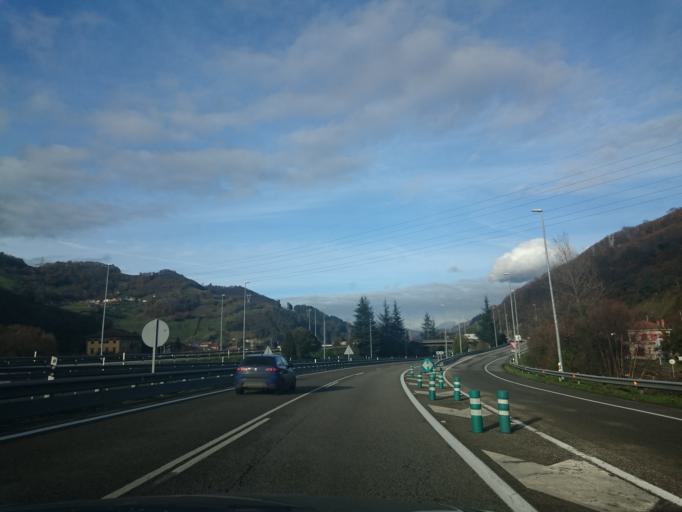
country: ES
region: Asturias
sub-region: Province of Asturias
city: Mieres
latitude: 43.1995
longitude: -5.7888
